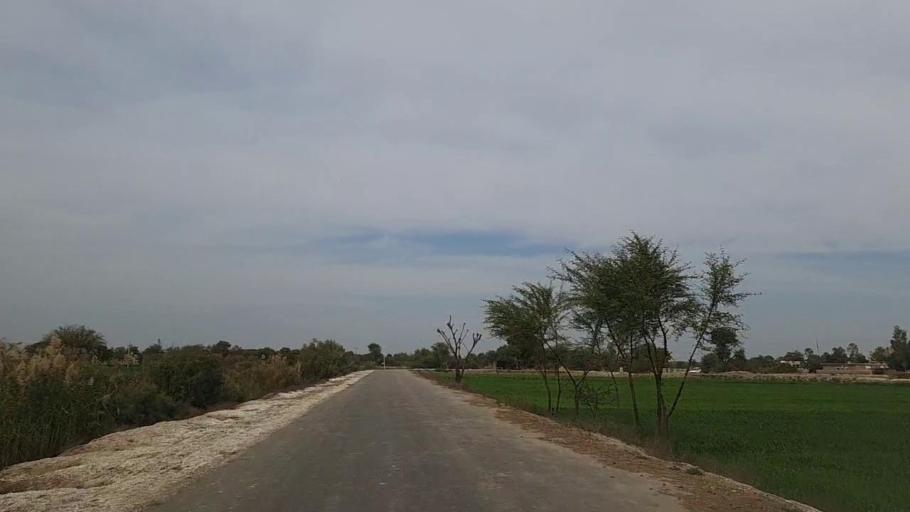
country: PK
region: Sindh
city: Daur
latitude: 26.4271
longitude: 68.4809
